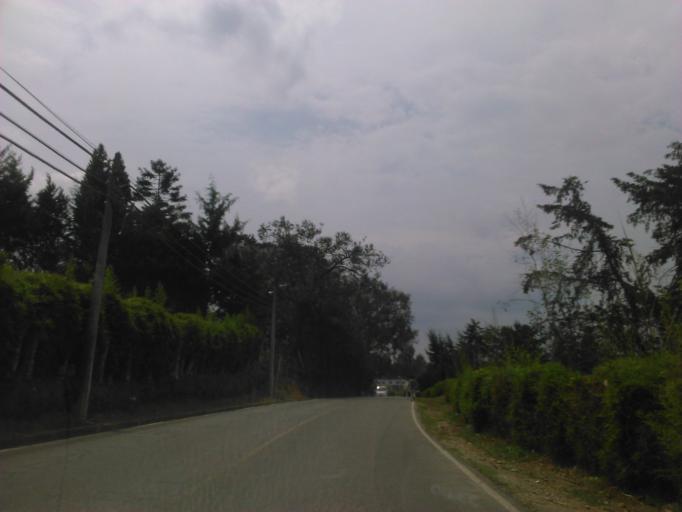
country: CO
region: Antioquia
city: San Vicente
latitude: 6.2321
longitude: -75.3833
